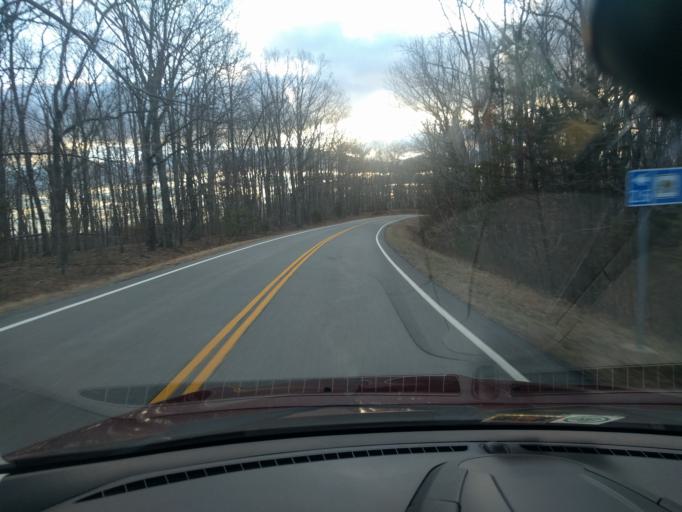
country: US
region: Virginia
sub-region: City of Bedford
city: Bedford
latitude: 37.4078
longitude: -79.5597
